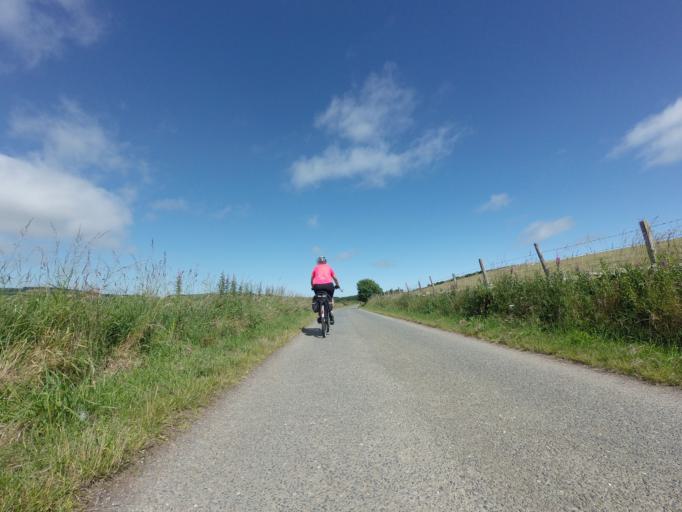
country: GB
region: Scotland
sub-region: Aberdeenshire
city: Banff
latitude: 57.6013
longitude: -2.5118
